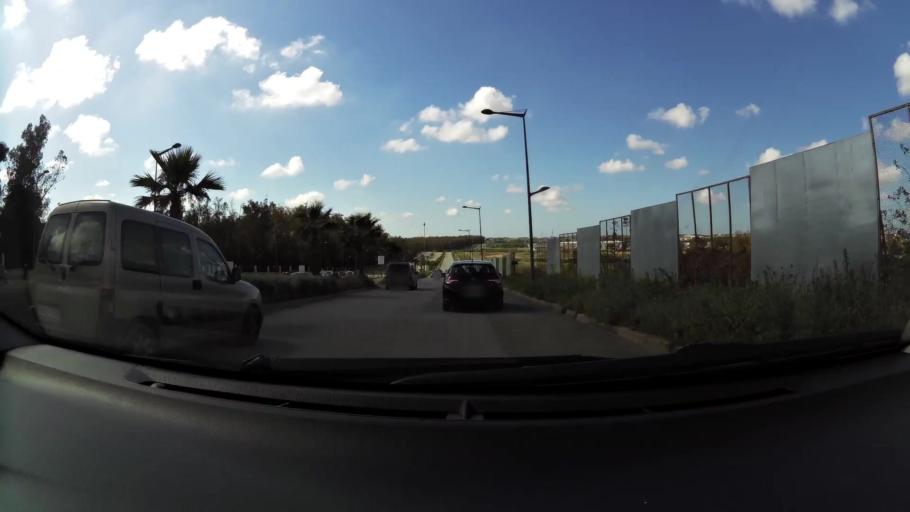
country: MA
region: Grand Casablanca
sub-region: Nouaceur
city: Bouskoura
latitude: 33.4725
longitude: -7.6154
